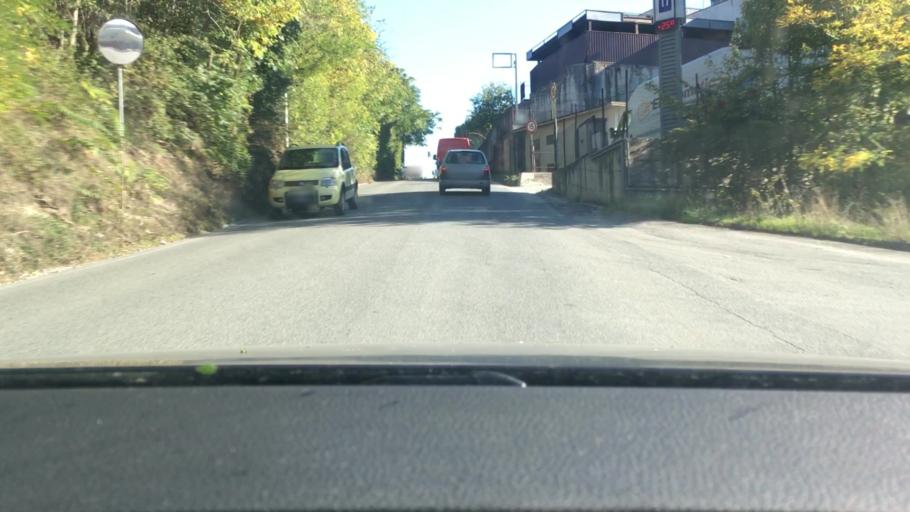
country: IT
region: The Marches
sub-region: Provincia di Ancona
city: Fabriano
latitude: 43.3519
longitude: 12.9217
